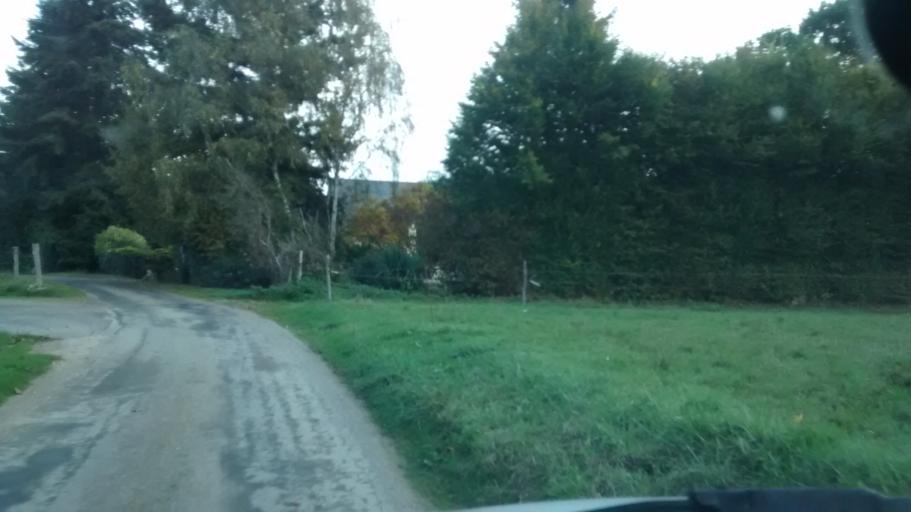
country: FR
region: Brittany
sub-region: Departement d'Ille-et-Vilaine
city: Servon-sur-Vilaine
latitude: 48.1295
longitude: -1.4741
